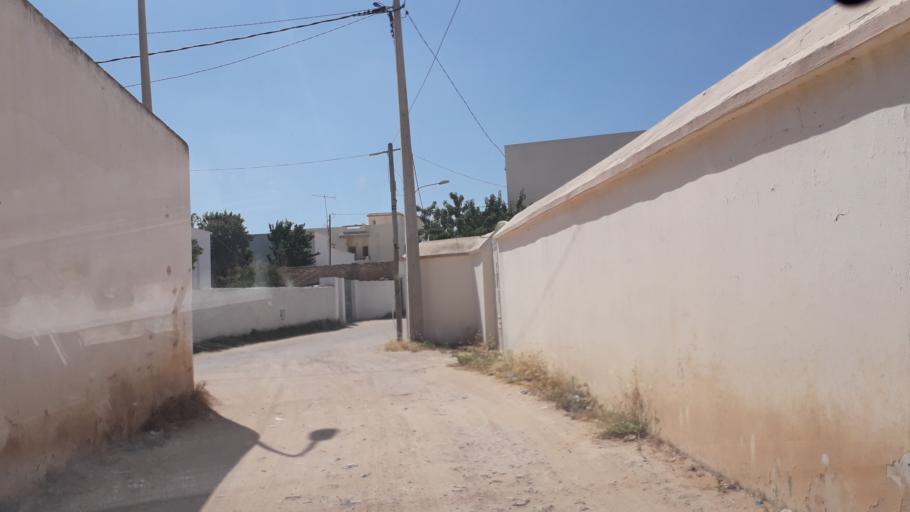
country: TN
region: Safaqis
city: Al Qarmadah
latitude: 34.8175
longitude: 10.7662
